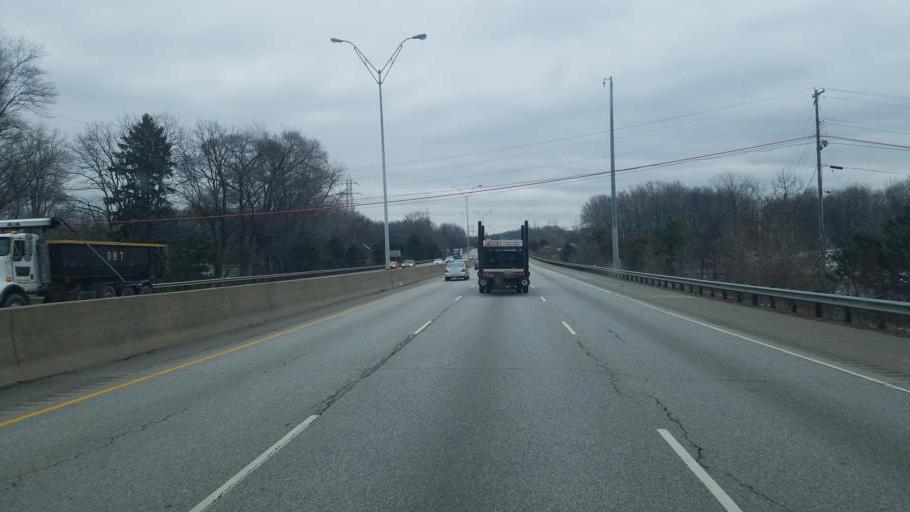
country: US
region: Ohio
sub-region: Summit County
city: Portage Lakes
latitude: 41.0266
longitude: -81.5386
